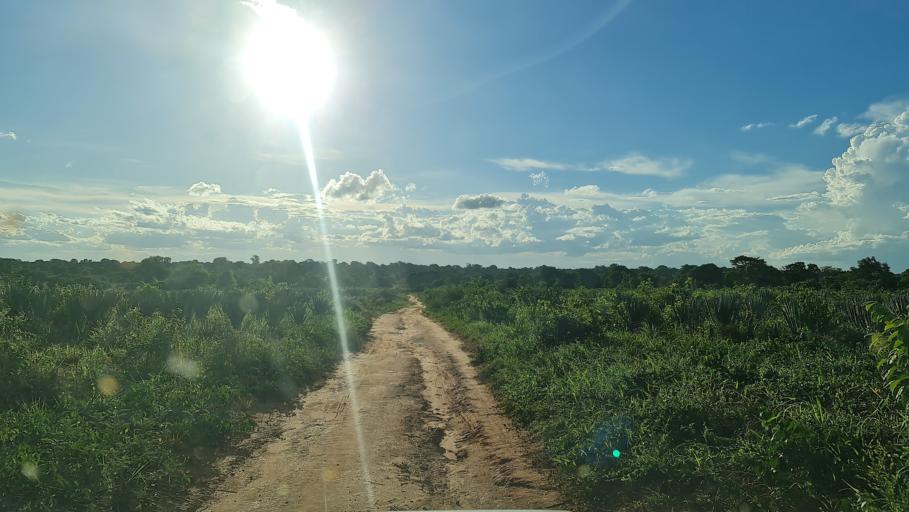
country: MZ
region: Nampula
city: Ilha de Mocambique
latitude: -14.9515
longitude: 40.1727
